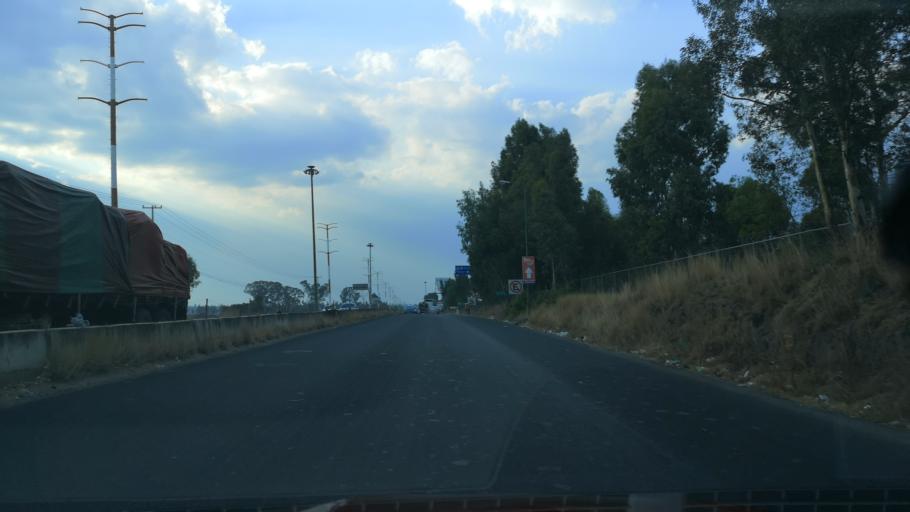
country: MX
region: Puebla
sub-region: Juan C. Bonilla
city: Santa Maria Zacatepec
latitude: 19.1293
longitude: -98.3709
